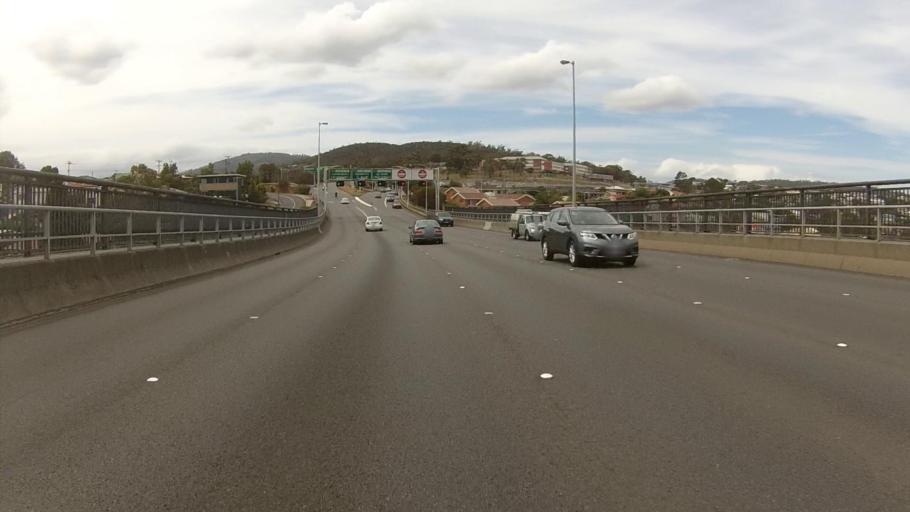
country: AU
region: Tasmania
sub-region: Clarence
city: Lindisfarne
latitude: -42.8638
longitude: 147.3518
